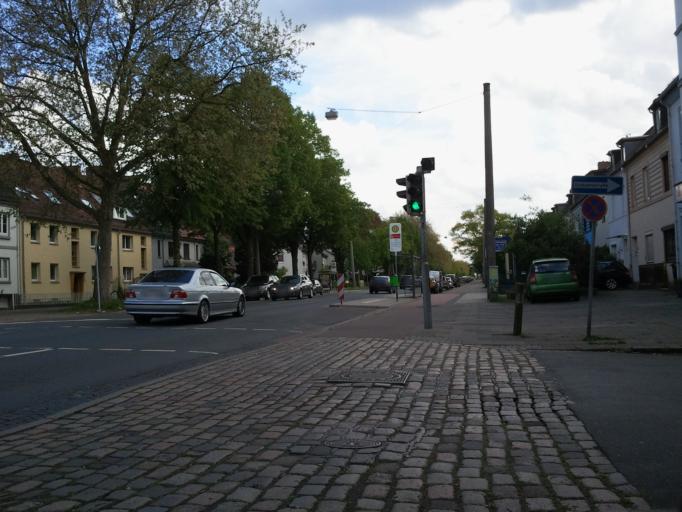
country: DE
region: Lower Saxony
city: Ritterhude
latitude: 53.1302
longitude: 8.7425
